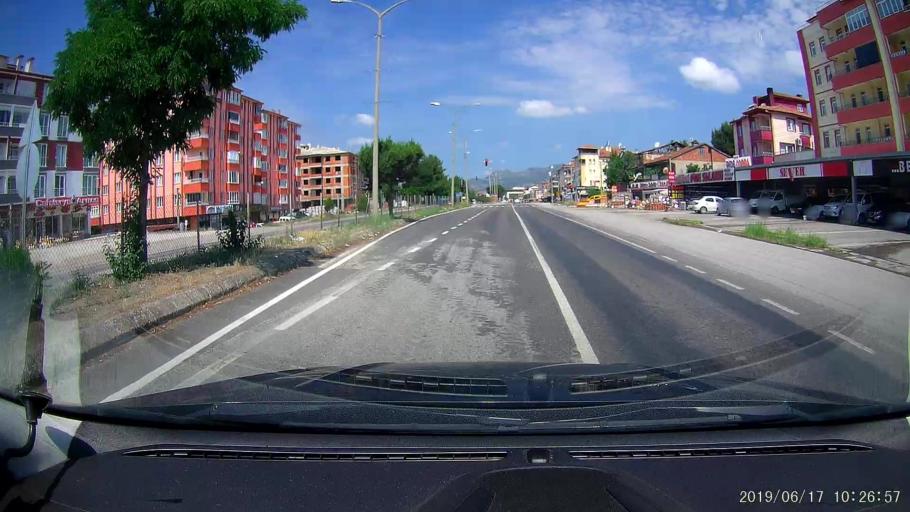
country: TR
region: Corum
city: Osmancik
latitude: 40.9762
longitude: 34.8129
